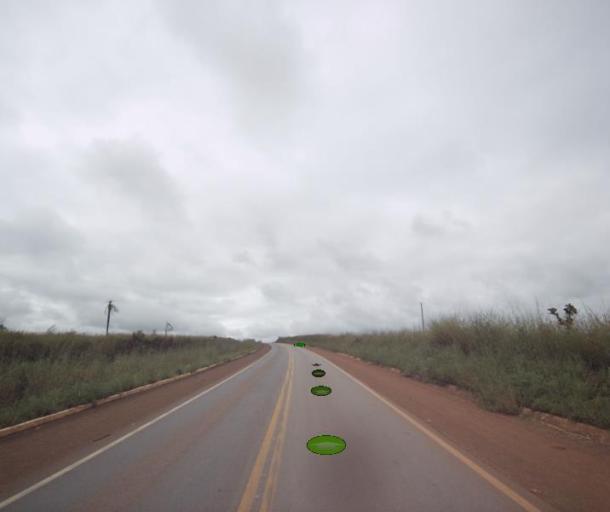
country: BR
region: Goias
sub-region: Uruacu
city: Uruacu
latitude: -14.6876
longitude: -49.1260
